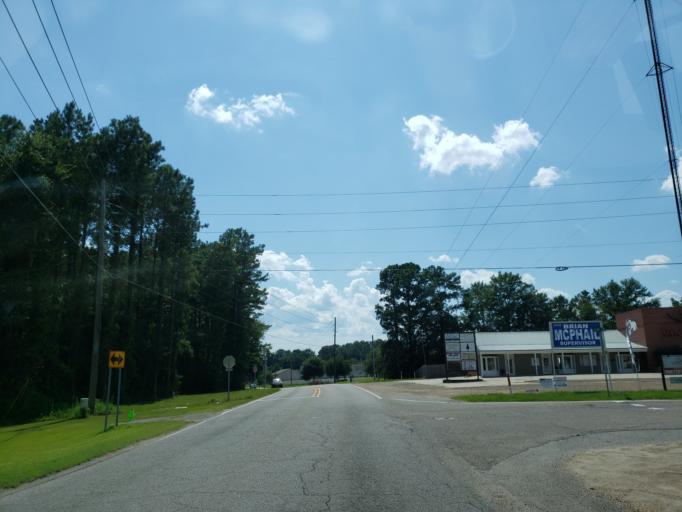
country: US
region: Mississippi
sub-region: Lamar County
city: West Hattiesburg
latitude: 31.2858
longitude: -89.4205
